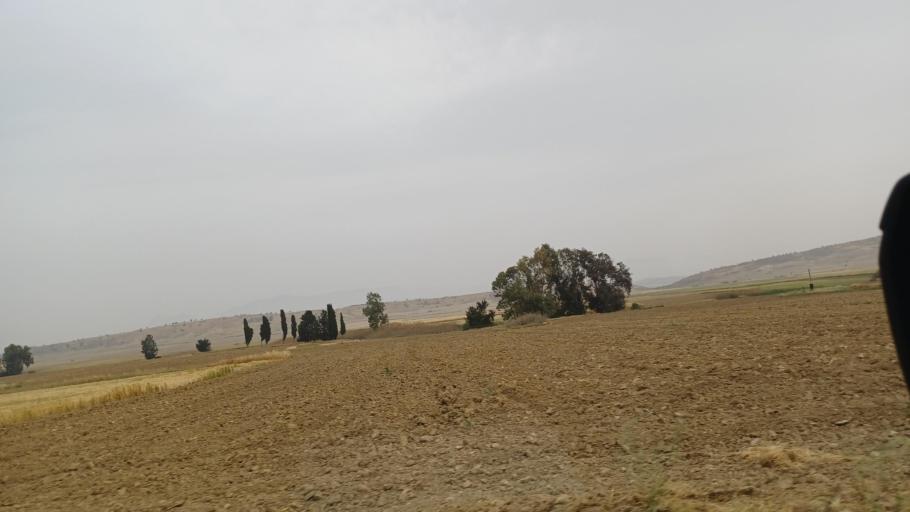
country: CY
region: Lefkosia
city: Mammari
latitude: 35.1853
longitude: 33.1807
